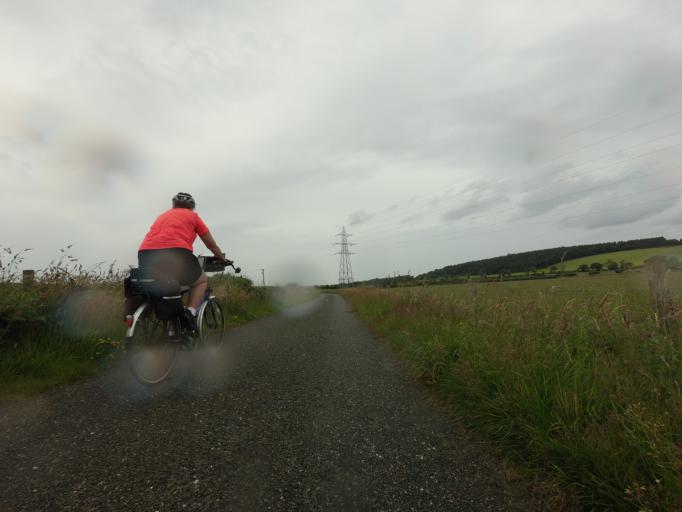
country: GB
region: Scotland
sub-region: Moray
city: Cullen
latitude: 57.6740
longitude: -2.7896
